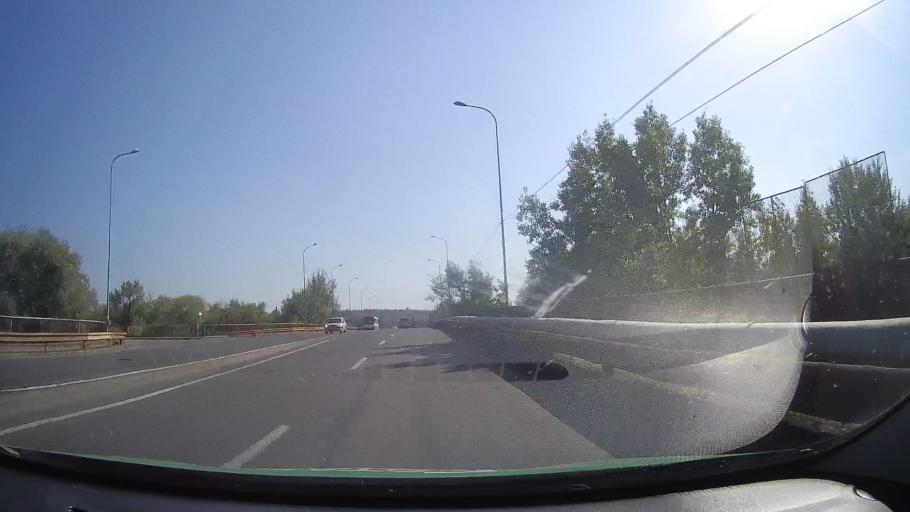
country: RO
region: Arad
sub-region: Oras Lipova
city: Radna
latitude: 46.0920
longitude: 21.6873
